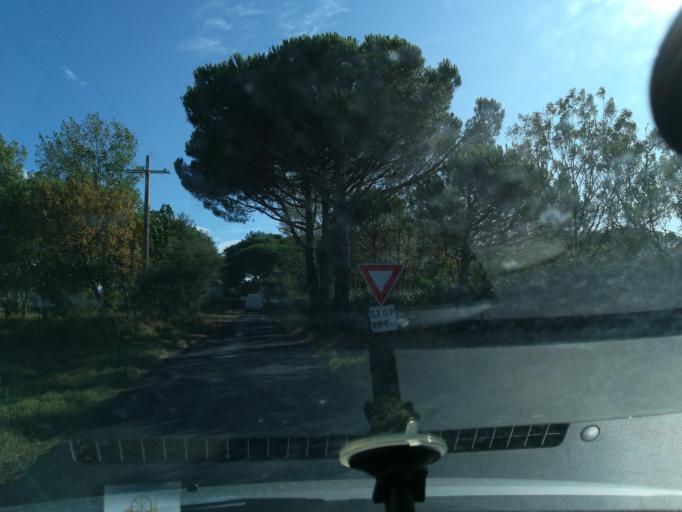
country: FR
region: Languedoc-Roussillon
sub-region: Departement de l'Herault
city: Portiragnes
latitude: 43.2883
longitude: 3.3728
